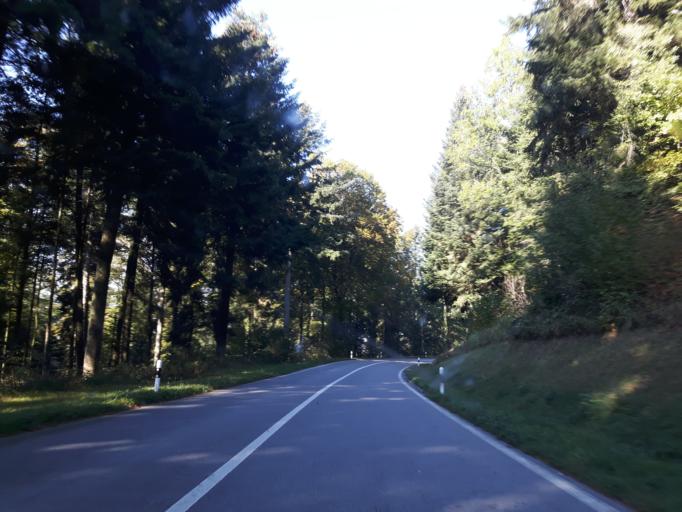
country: CH
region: Bern
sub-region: Oberaargau
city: Roggwil
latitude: 47.2395
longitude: 7.8403
